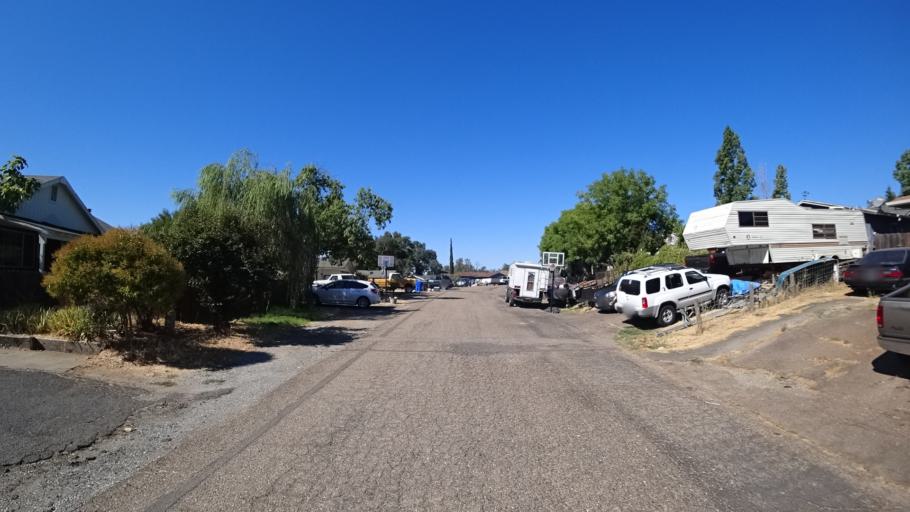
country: US
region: California
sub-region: Calaveras County
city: Murphys
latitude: 38.1093
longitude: -120.4584
